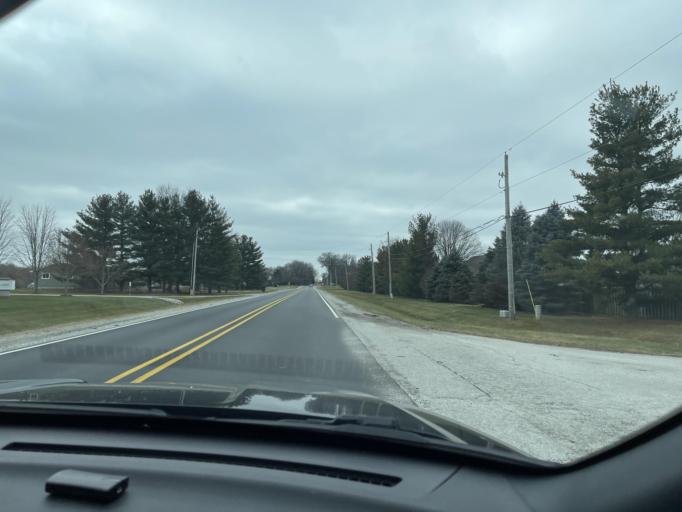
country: US
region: Illinois
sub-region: Sangamon County
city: Leland Grove
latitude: 39.7971
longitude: -89.7392
